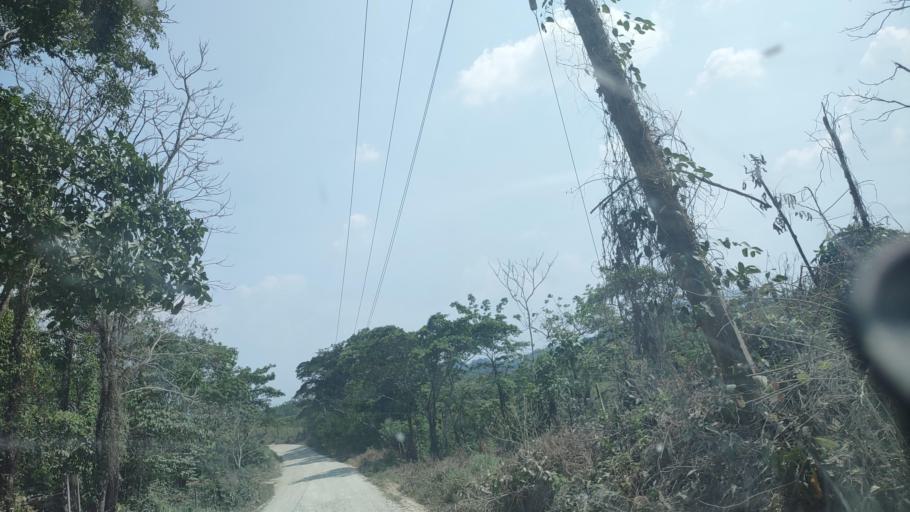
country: MX
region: Tabasco
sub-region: Huimanguillo
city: Francisco Rueda
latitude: 17.5838
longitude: -93.8921
